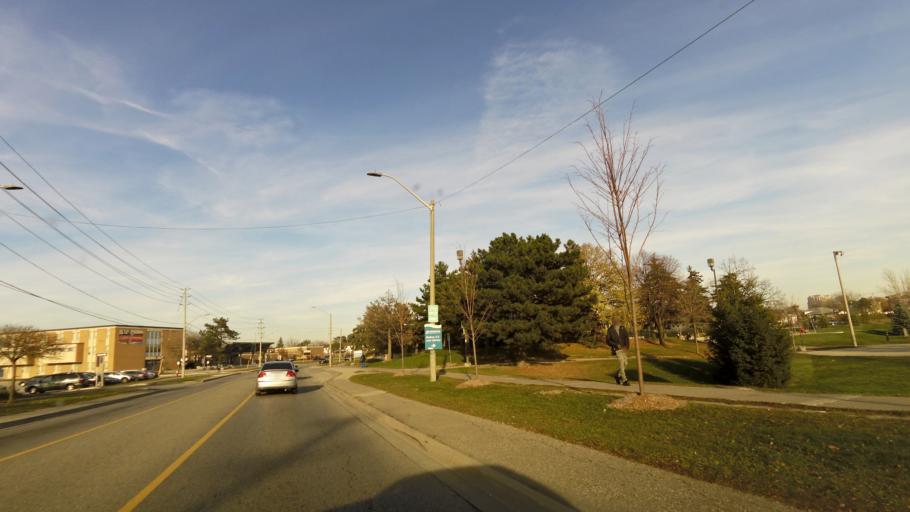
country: CA
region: Ontario
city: Etobicoke
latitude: 43.7225
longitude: -79.6406
